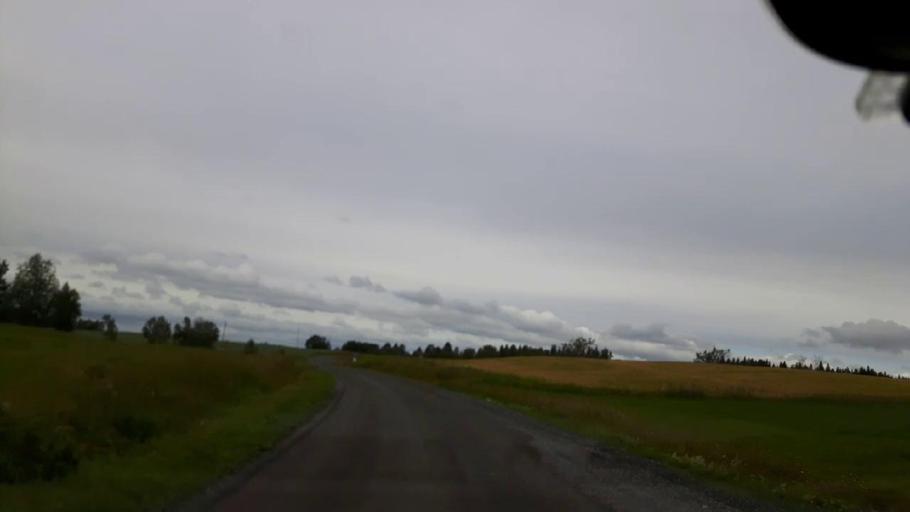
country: SE
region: Jaemtland
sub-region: Krokoms Kommun
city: Krokom
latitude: 63.3061
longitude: 14.3390
